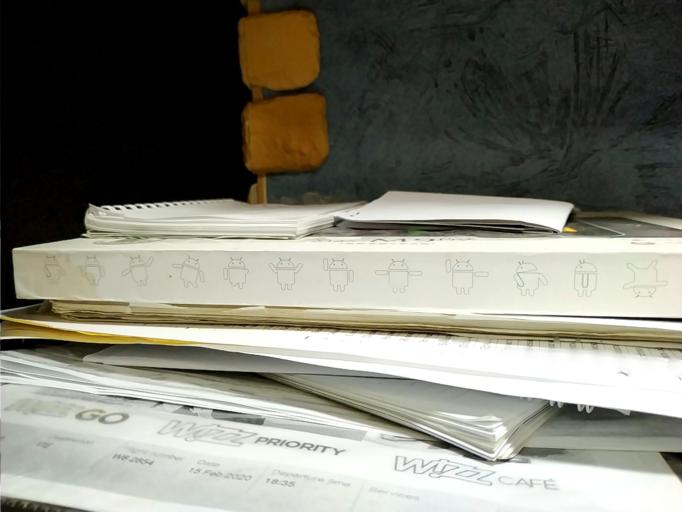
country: RU
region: Arkhangelskaya
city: Onega
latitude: 63.1388
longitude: 38.3583
